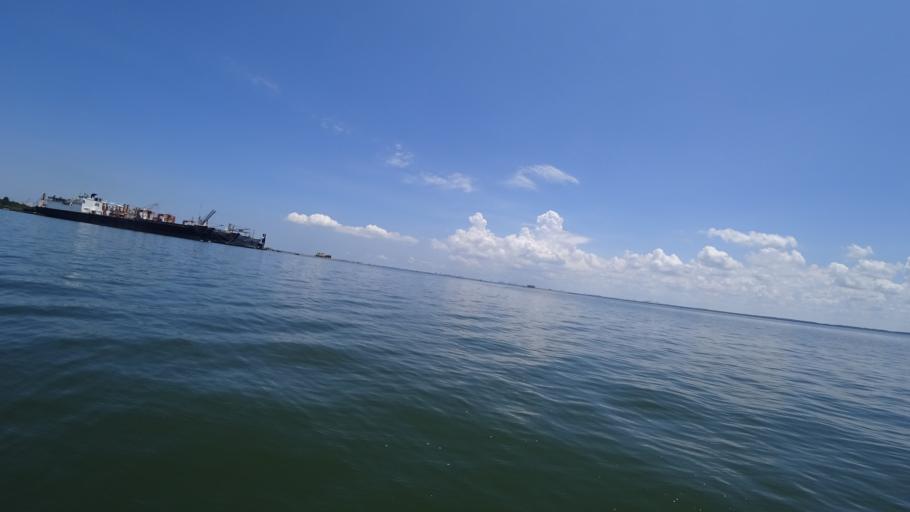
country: US
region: Virginia
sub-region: City of Newport News
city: Newport News
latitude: 36.9602
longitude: -76.4268
